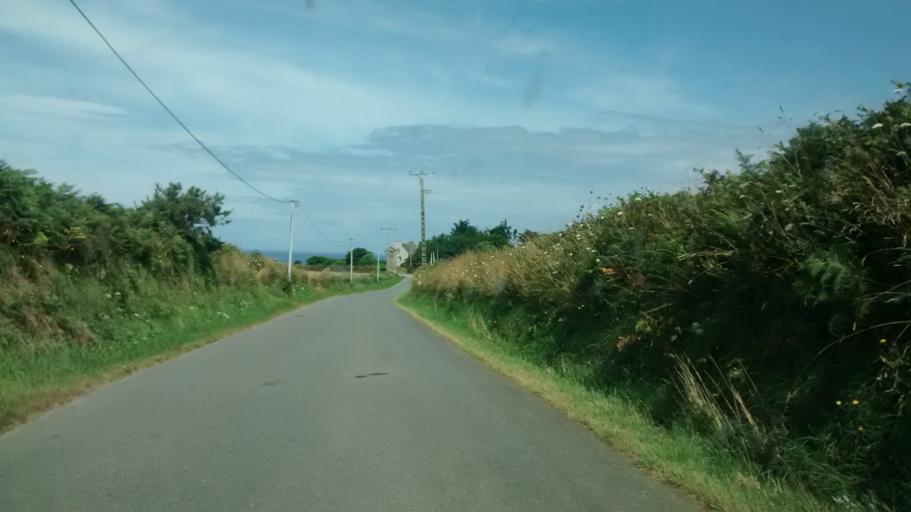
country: FR
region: Brittany
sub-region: Departement du Finistere
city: Plouguerneau
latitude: 48.6139
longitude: -4.4798
